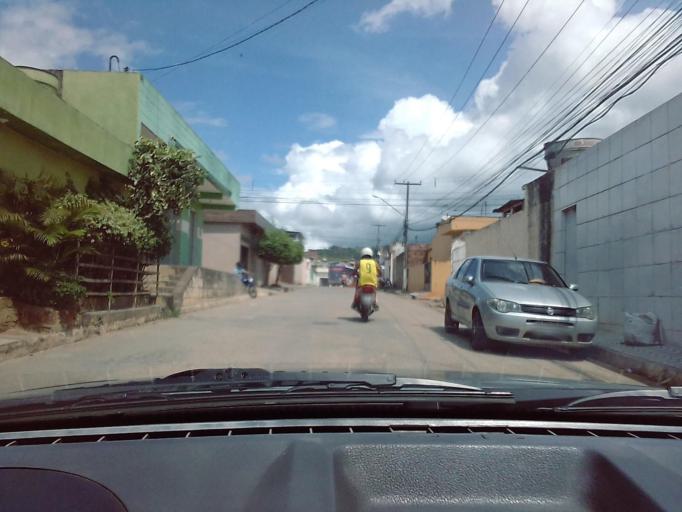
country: BR
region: Pernambuco
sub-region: Vitoria De Santo Antao
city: Vitoria de Santo Antao
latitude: -8.1268
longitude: -35.2929
